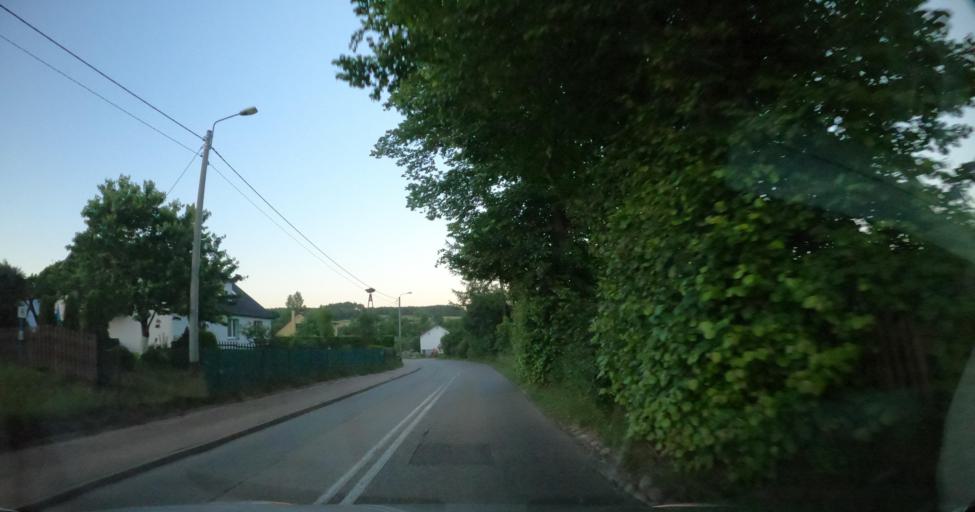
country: PL
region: Pomeranian Voivodeship
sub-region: Powiat wejherowski
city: Linia
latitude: 54.4626
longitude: 17.9730
